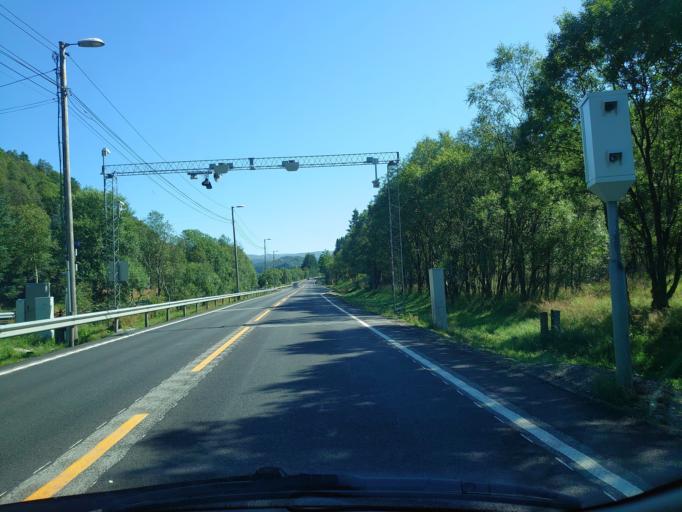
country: NO
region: Hordaland
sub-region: Bergen
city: Hylkje
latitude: 60.4696
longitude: 5.3699
